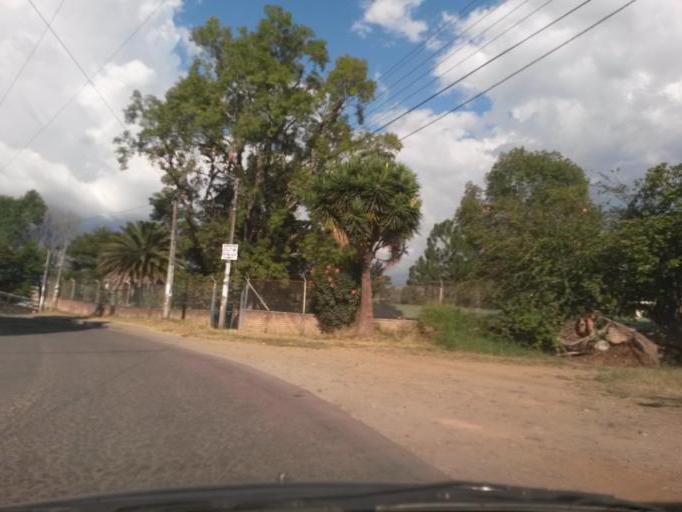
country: CO
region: Cauca
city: Popayan
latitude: 2.4335
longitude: -76.6153
